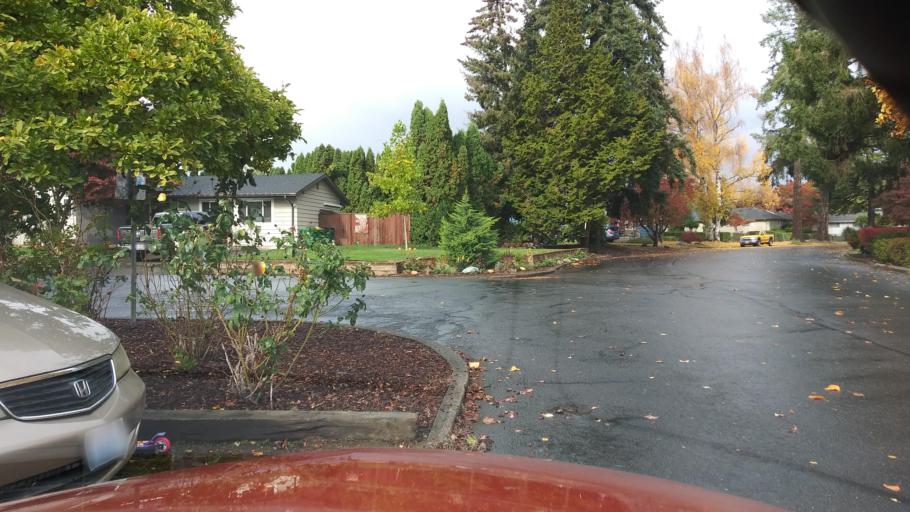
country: US
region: Oregon
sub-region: Washington County
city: Forest Grove
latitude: 45.5120
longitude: -123.0979
